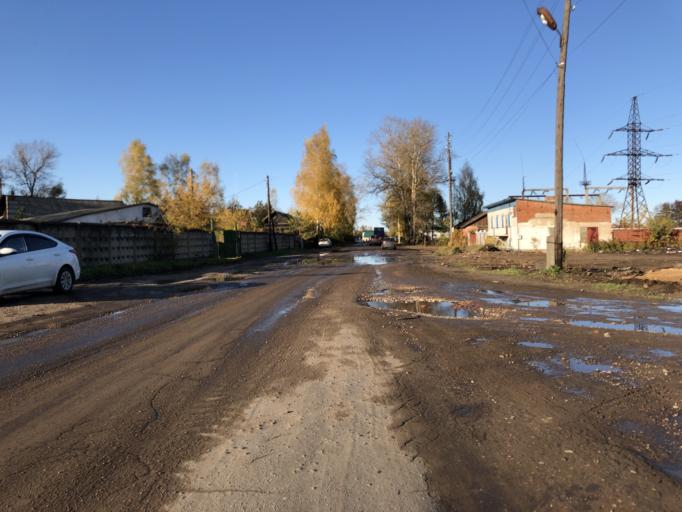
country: RU
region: Tverskaya
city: Rzhev
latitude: 56.2387
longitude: 34.3460
